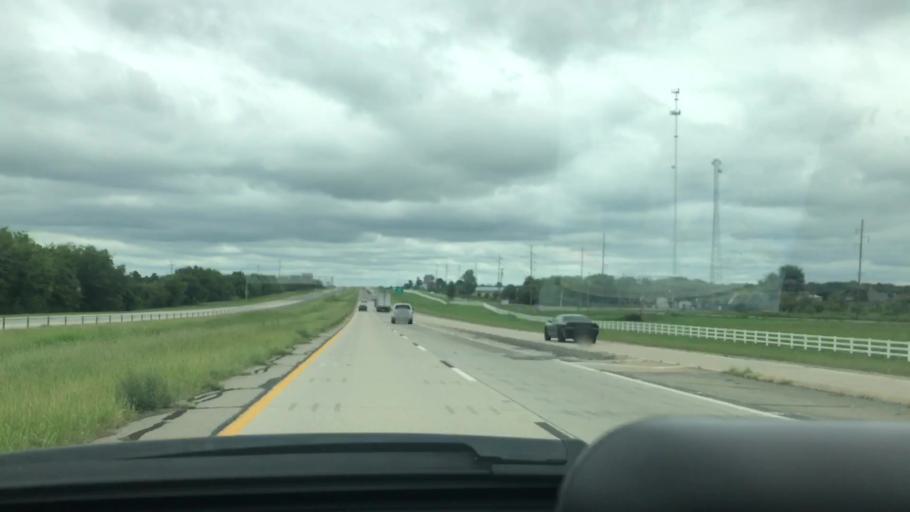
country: US
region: Oklahoma
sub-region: McIntosh County
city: Checotah
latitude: 35.4621
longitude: -95.5422
